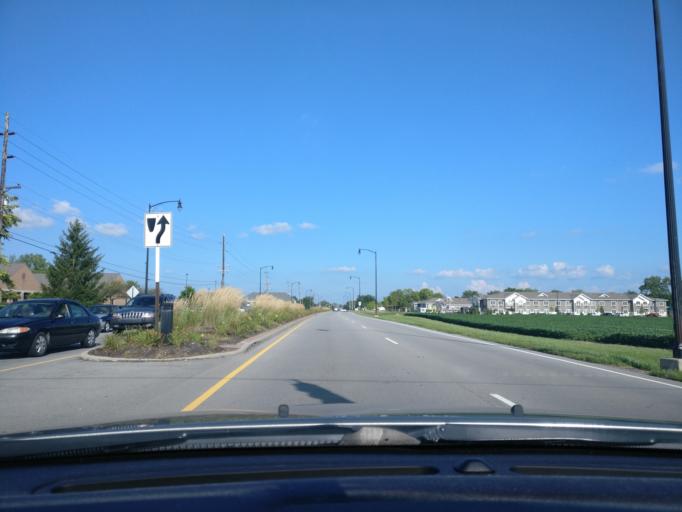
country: US
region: Ohio
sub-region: Warren County
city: Springboro
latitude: 39.5606
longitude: -84.2471
